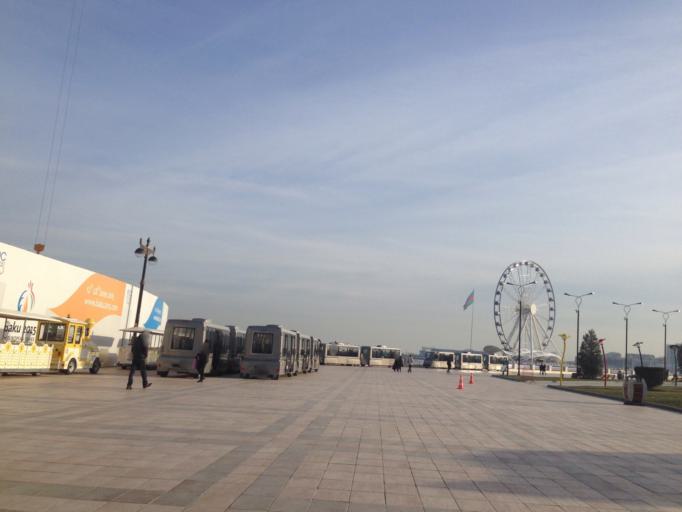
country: AZ
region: Baki
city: Badamdar
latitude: 40.3579
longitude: 49.8359
